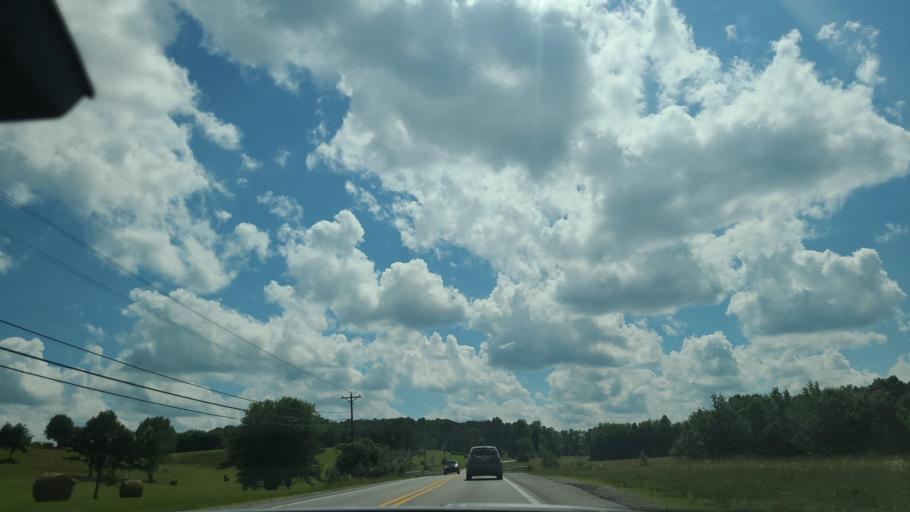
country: US
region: Kentucky
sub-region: Whitley County
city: Corbin
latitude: 36.9006
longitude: -84.1734
